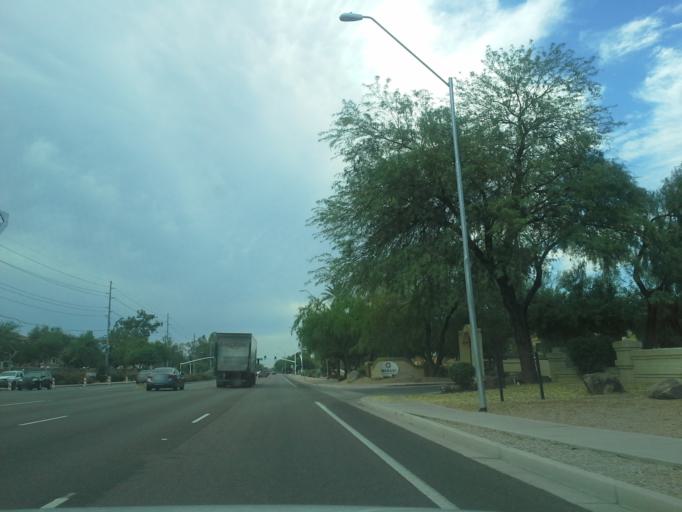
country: US
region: Arizona
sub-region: Maricopa County
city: Paradise Valley
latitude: 33.5772
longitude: -111.9262
